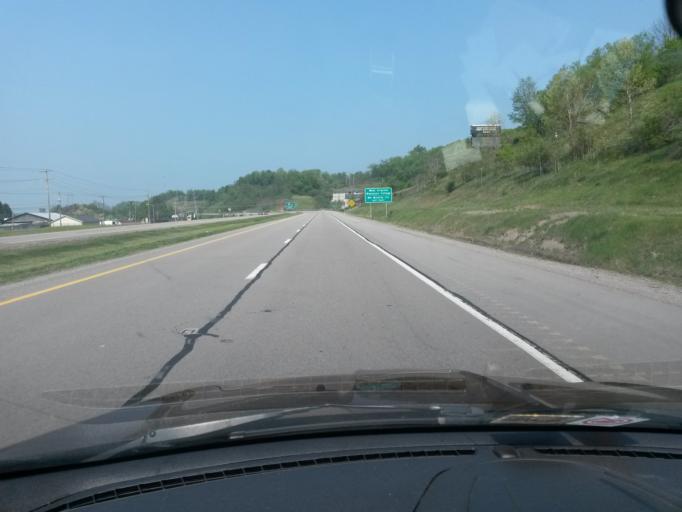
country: US
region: West Virginia
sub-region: Upshur County
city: Buckhannon
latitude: 39.0021
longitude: -80.2220
